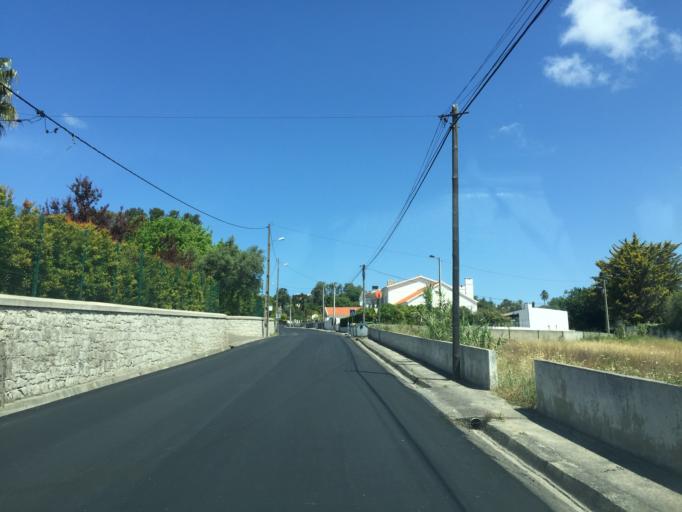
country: PT
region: Lisbon
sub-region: Sintra
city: Sintra
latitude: 38.8086
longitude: -9.4015
